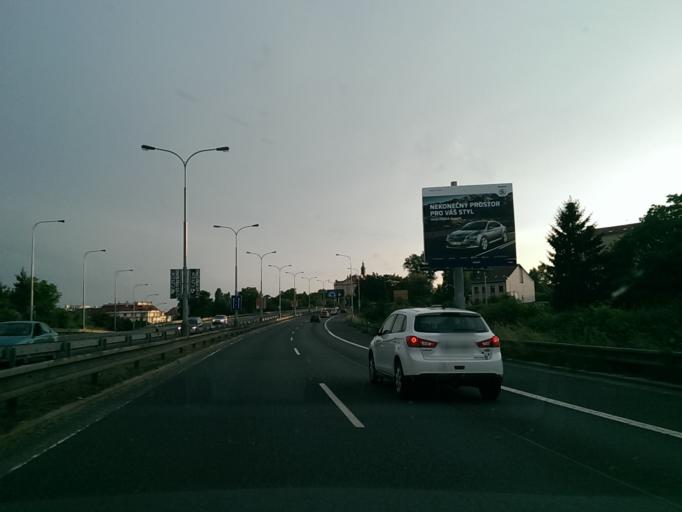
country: CZ
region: Praha
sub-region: Praha 8
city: Liben
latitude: 50.1192
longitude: 14.4720
